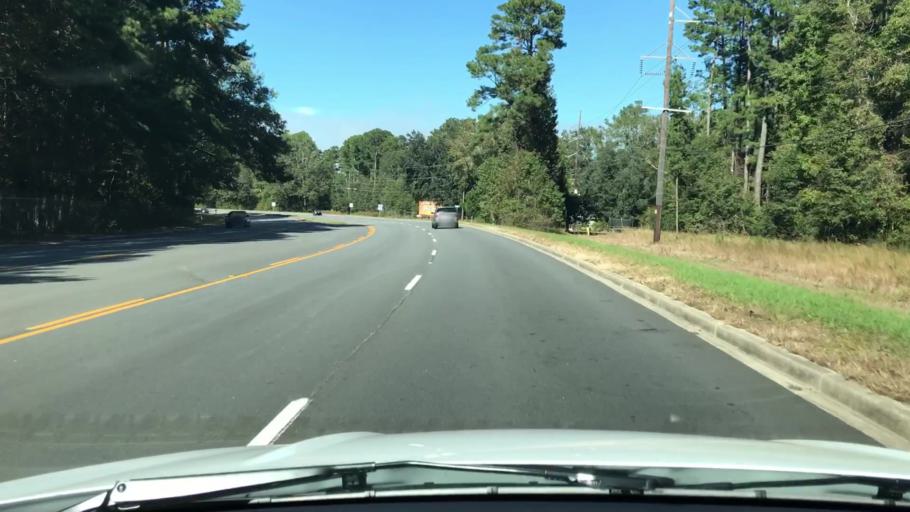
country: US
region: South Carolina
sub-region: Beaufort County
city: Laurel Bay
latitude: 32.5837
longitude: -80.7429
